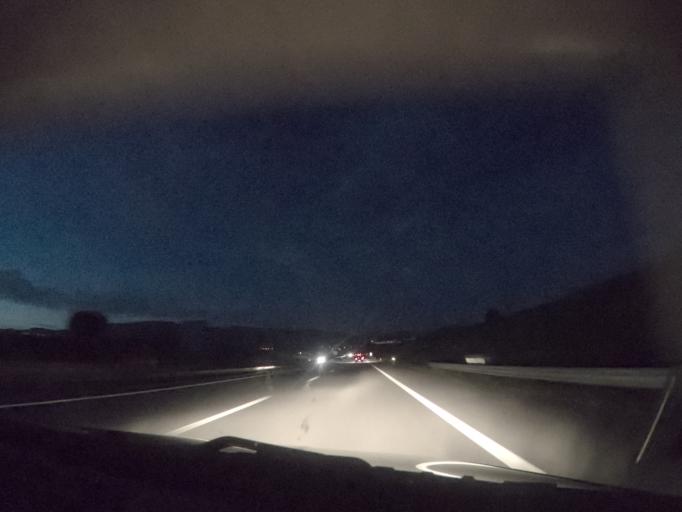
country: PT
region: Guarda
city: Alcains
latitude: 39.9978
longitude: -7.4623
